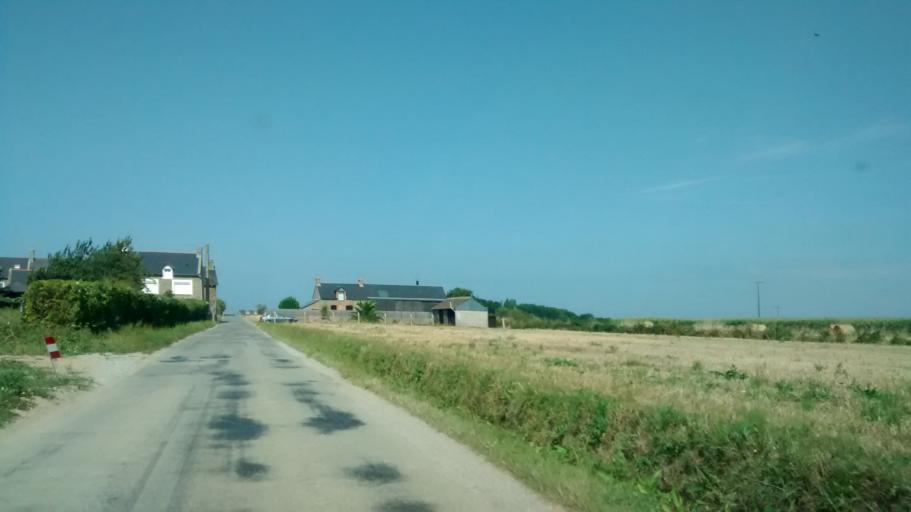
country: FR
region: Brittany
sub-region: Departement d'Ille-et-Vilaine
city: Saint-Coulomb
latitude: 48.6778
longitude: -1.8985
